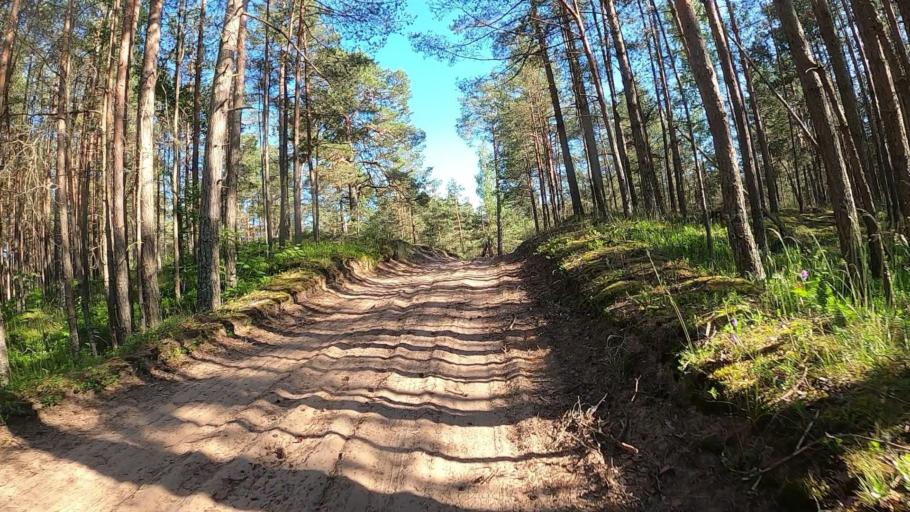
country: LV
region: Carnikava
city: Carnikava
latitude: 57.1013
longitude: 24.2351
